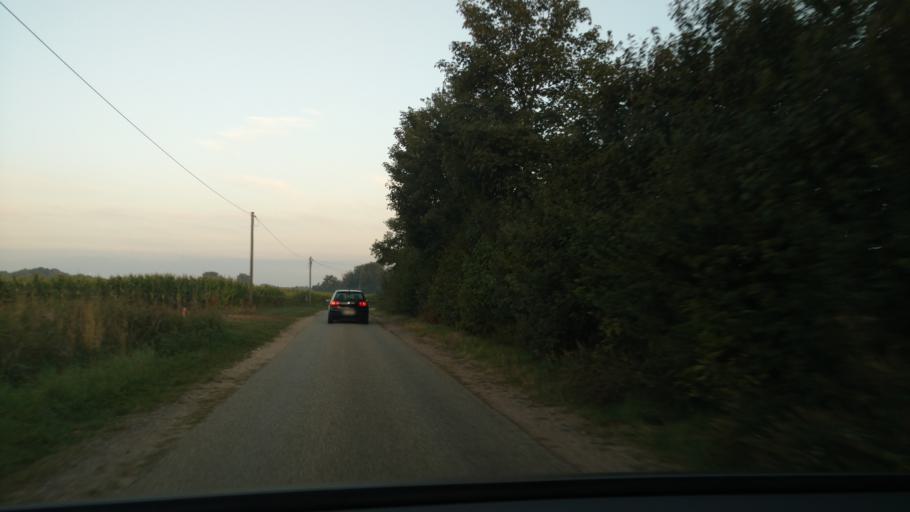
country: DE
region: North Rhine-Westphalia
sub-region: Regierungsbezirk Munster
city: Velen
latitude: 51.8582
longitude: 6.9848
